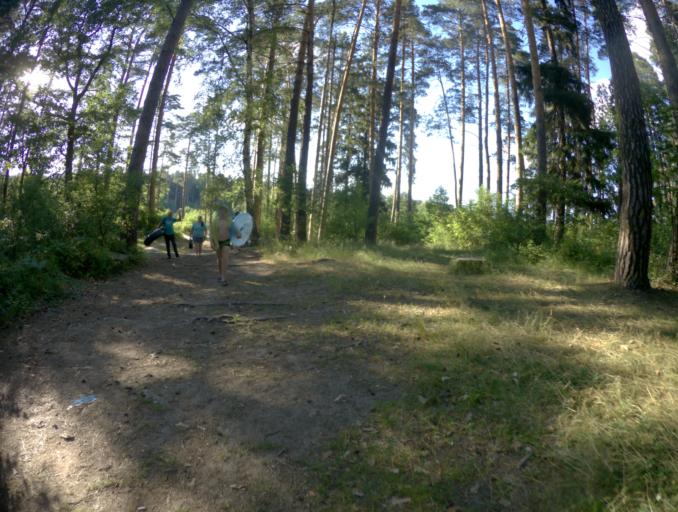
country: RU
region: Nizjnij Novgorod
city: Taremskoye
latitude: 56.0146
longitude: 42.9622
